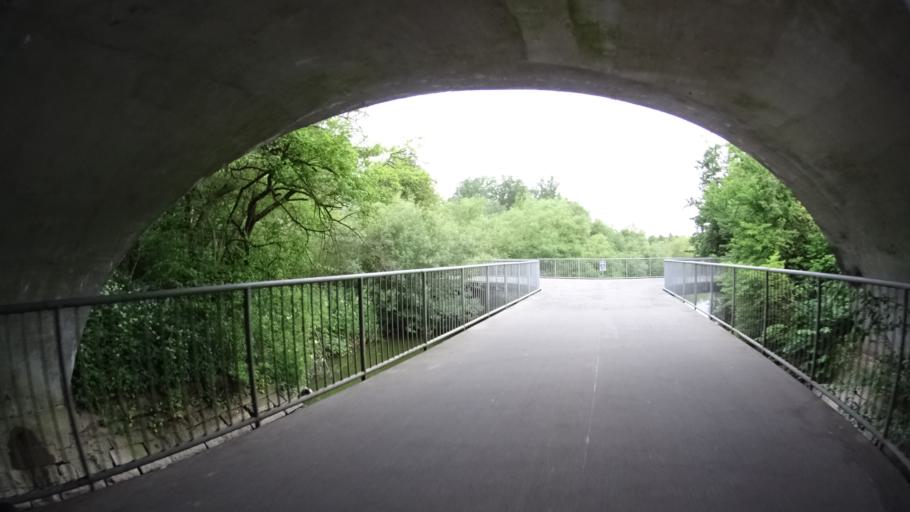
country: DK
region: Central Jutland
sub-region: Arhus Kommune
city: Arhus
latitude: 56.1439
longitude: 10.1734
